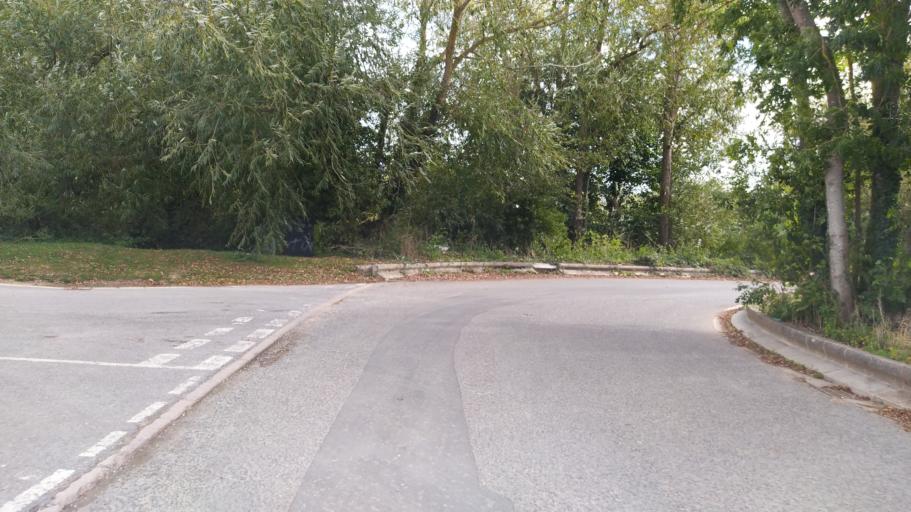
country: GB
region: England
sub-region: Reading
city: Reading
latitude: 51.4248
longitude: -0.9991
